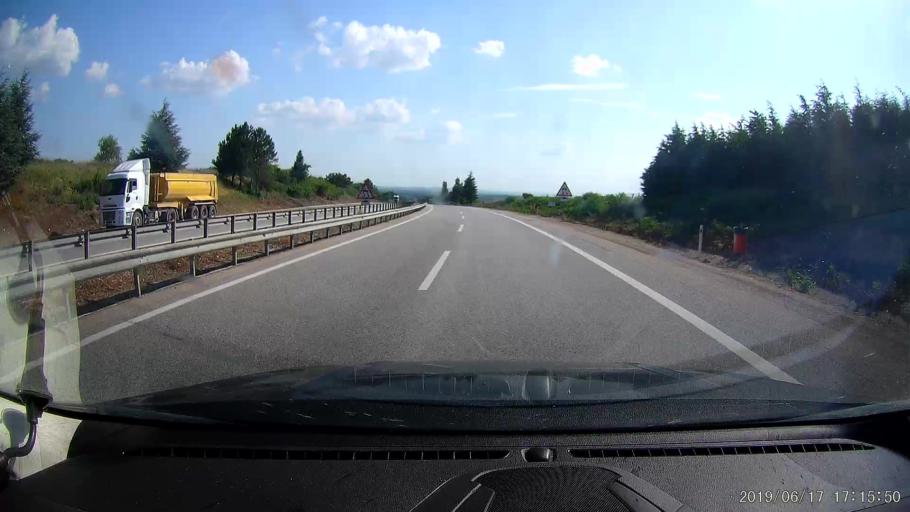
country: GR
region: East Macedonia and Thrace
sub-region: Nomos Evrou
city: Kastanies
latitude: 41.7003
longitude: 26.4886
